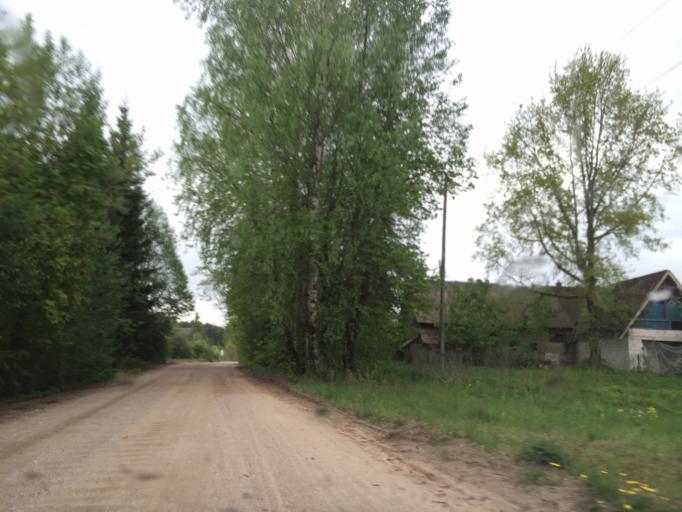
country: LV
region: Ogre
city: Ogre
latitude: 56.8254
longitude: 24.6524
